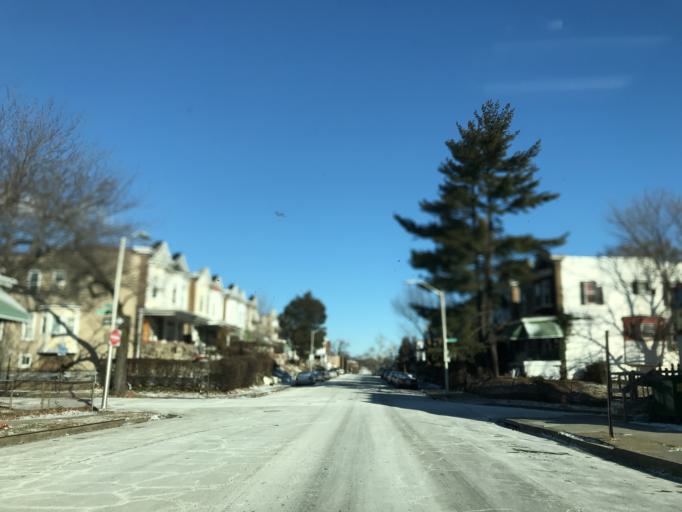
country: US
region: Maryland
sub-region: Baltimore County
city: Charlestown
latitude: 39.3032
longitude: -76.6654
